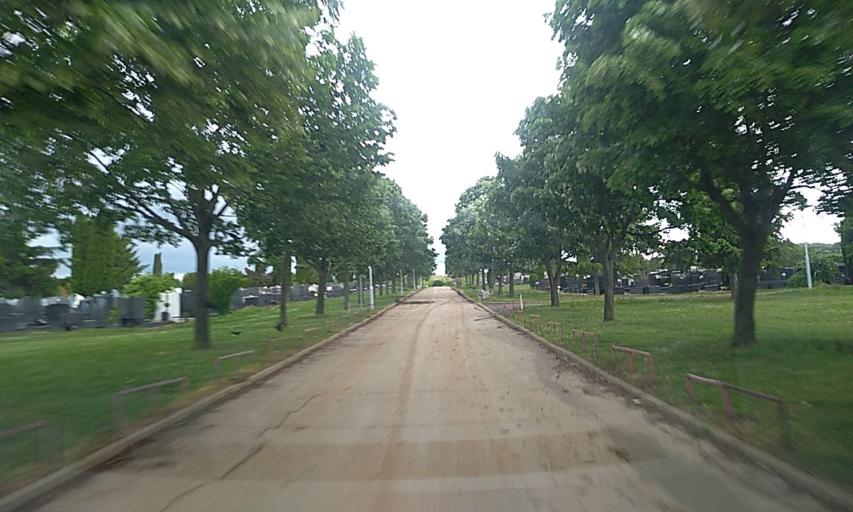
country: RS
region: Central Serbia
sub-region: Nisavski Okrug
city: Nis
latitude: 43.2940
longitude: 21.8835
